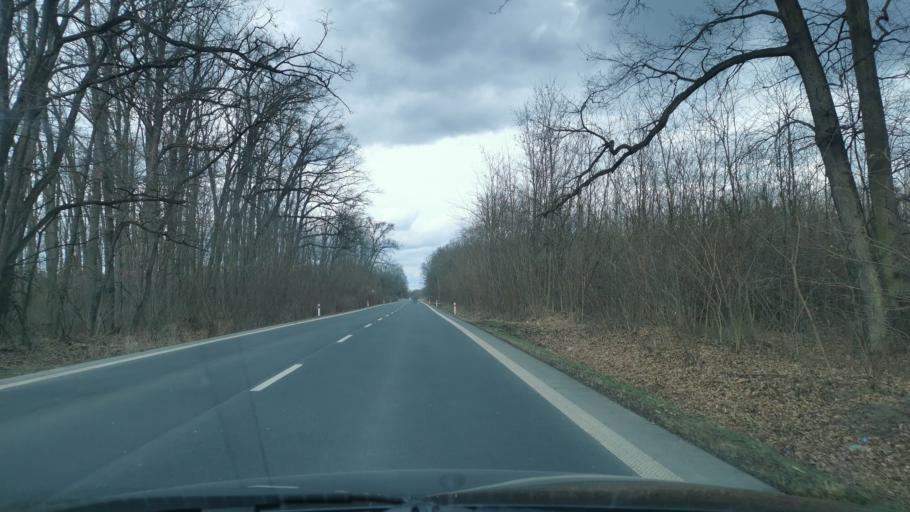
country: SK
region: Trnavsky
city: Gbely
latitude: 48.7540
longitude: 17.0764
